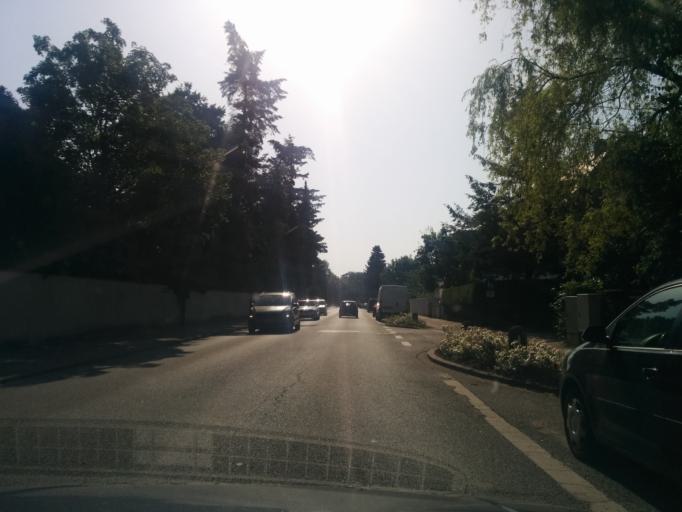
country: DE
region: Bavaria
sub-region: Upper Bavaria
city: Grunwald
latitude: 48.0381
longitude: 11.5313
